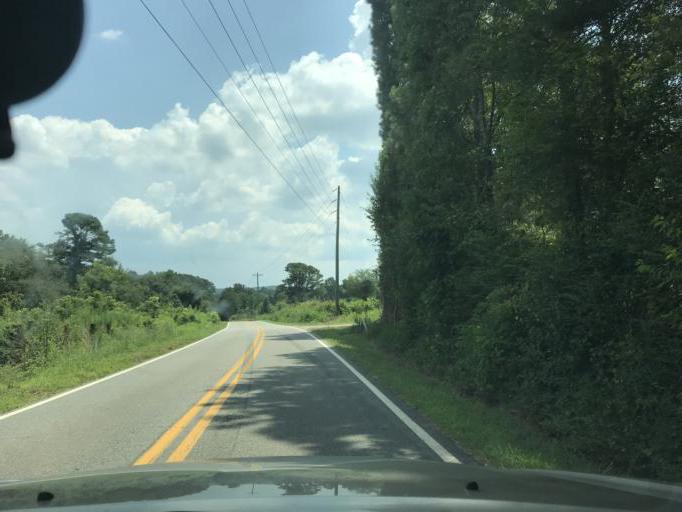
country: US
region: Georgia
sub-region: Forsyth County
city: Cumming
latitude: 34.2664
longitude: -84.1555
